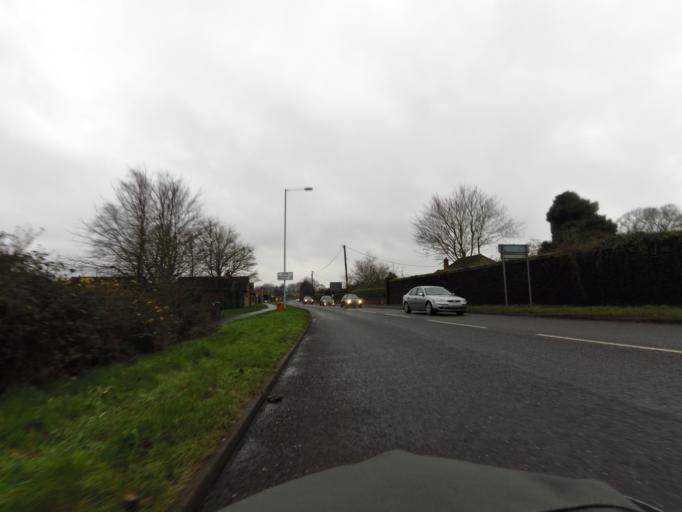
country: GB
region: England
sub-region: Norfolk
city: Briston
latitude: 52.9025
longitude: 1.0884
